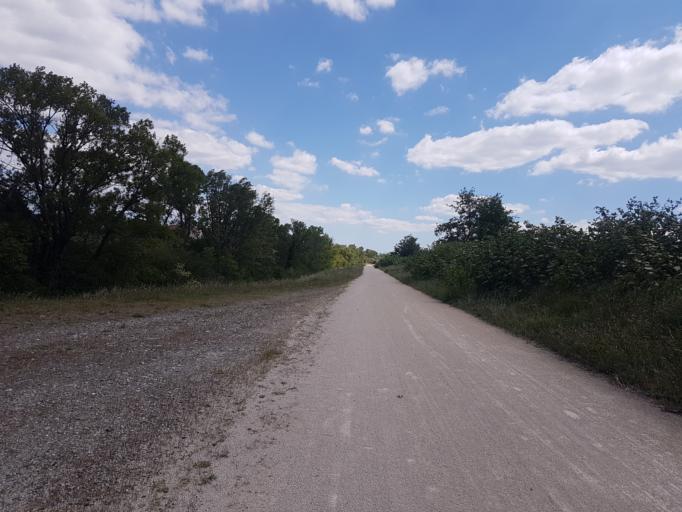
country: FR
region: Rhone-Alpes
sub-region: Departement de la Drome
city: La Roche-de-Glun
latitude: 45.0198
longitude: 4.8499
